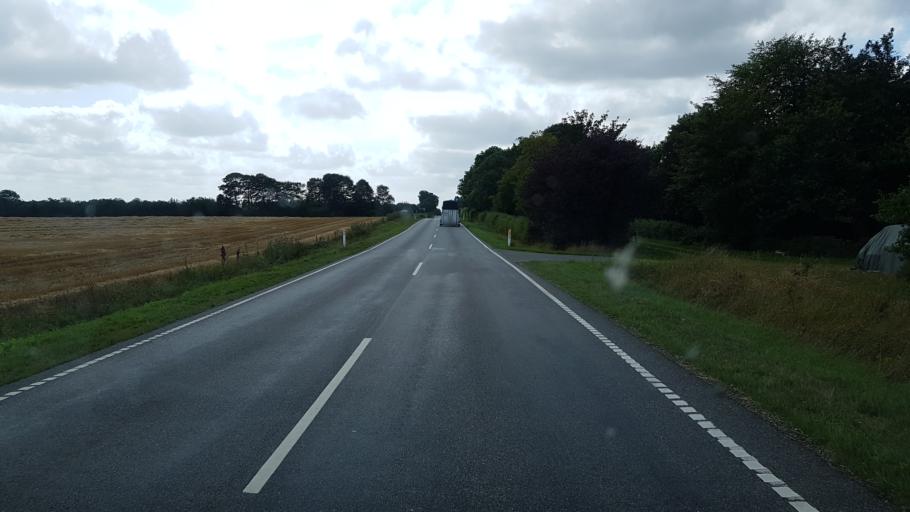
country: DK
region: South Denmark
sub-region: Vejen Kommune
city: Brorup
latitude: 55.5358
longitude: 9.0569
